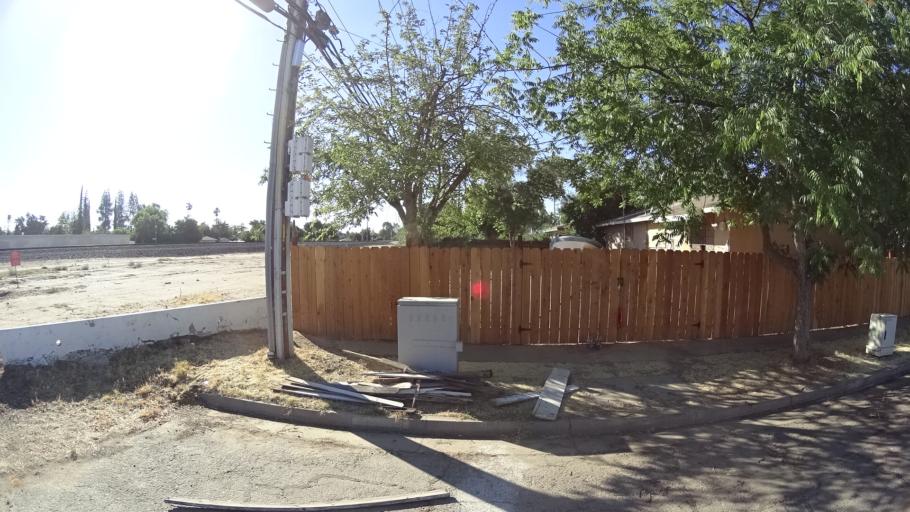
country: US
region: California
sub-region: Fresno County
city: Fresno
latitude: 36.7948
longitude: -119.8212
